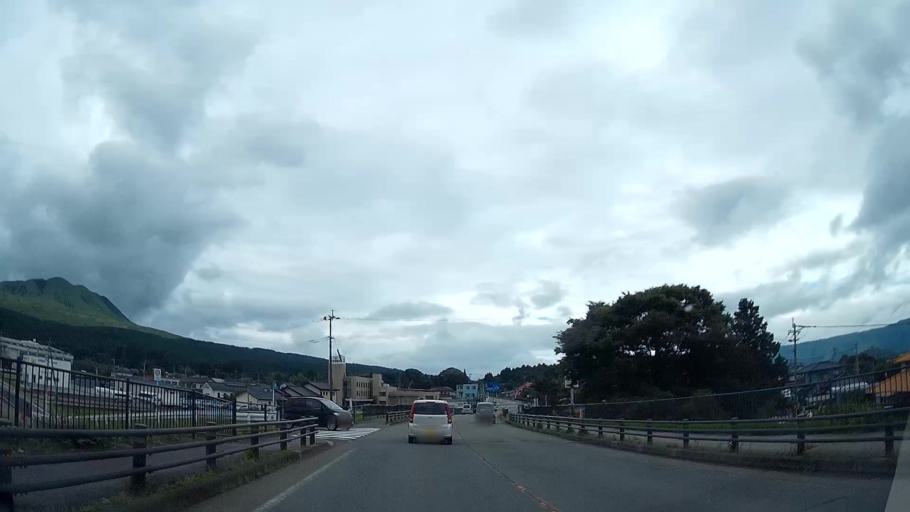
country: JP
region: Kumamoto
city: Aso
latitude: 32.9364
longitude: 131.0827
